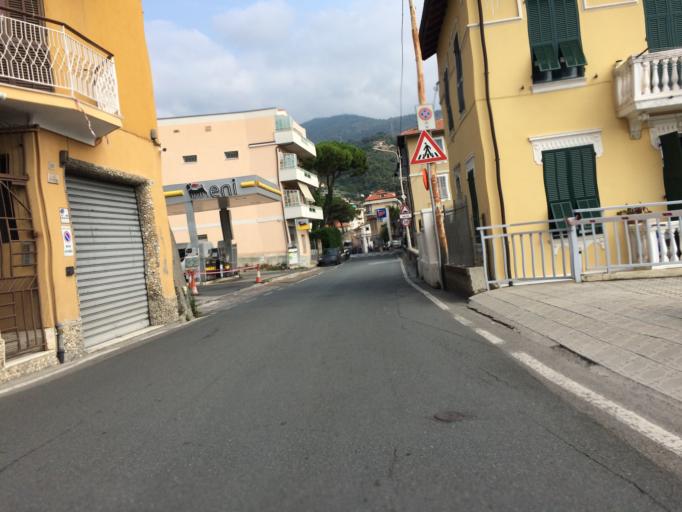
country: IT
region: Liguria
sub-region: Provincia di Imperia
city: San Remo
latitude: 43.8253
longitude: 7.7716
